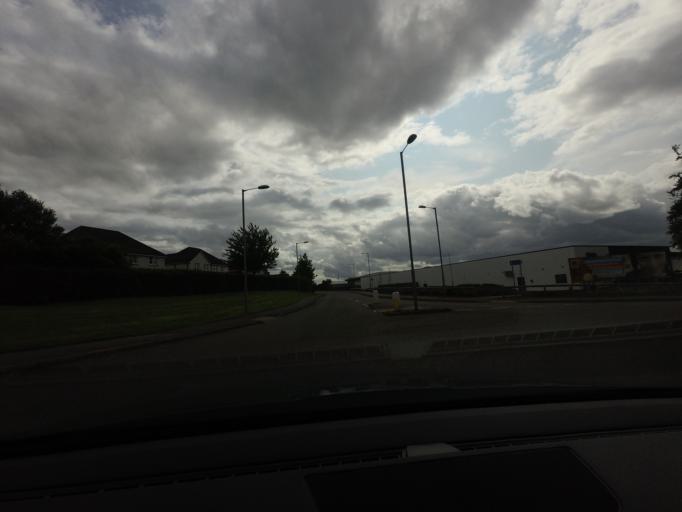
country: GB
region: Scotland
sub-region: Highland
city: Inverness
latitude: 57.4688
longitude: -4.1877
